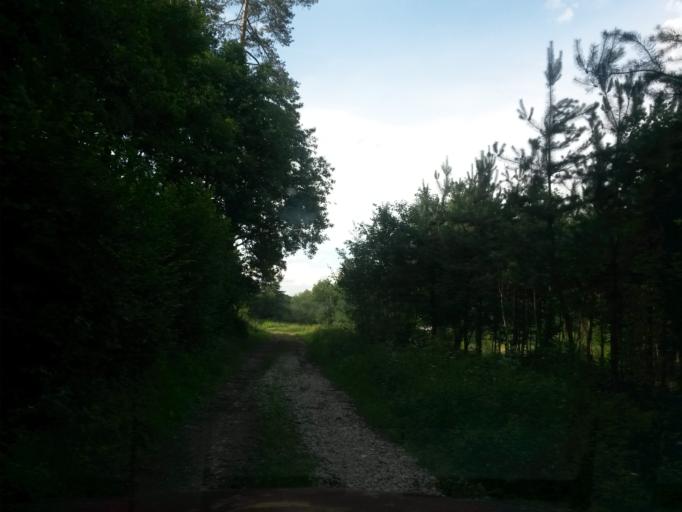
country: SK
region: Kosicky
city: Moldava nad Bodvou
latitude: 48.6151
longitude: 21.1125
